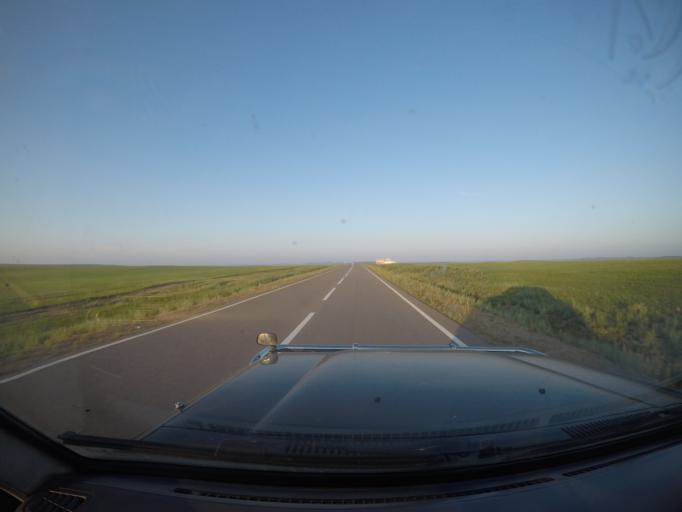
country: MN
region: Suhbaatar
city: Hanhohiy
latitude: 47.5713
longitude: 112.3083
